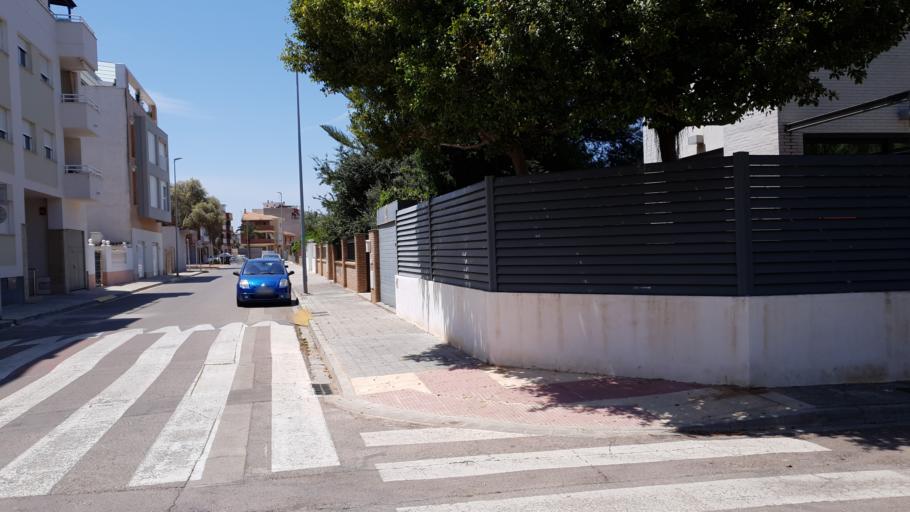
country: ES
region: Valencia
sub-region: Provincia de Castello
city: Burriana
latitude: 39.8662
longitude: -0.0742
